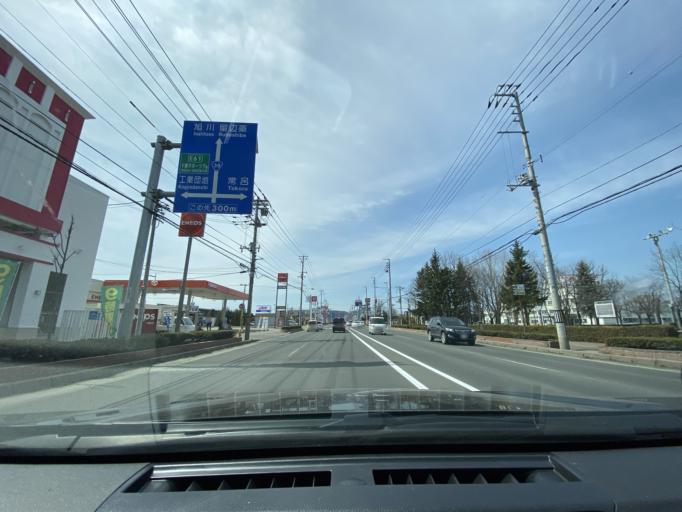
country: JP
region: Hokkaido
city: Kitami
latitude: 43.7982
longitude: 143.8608
